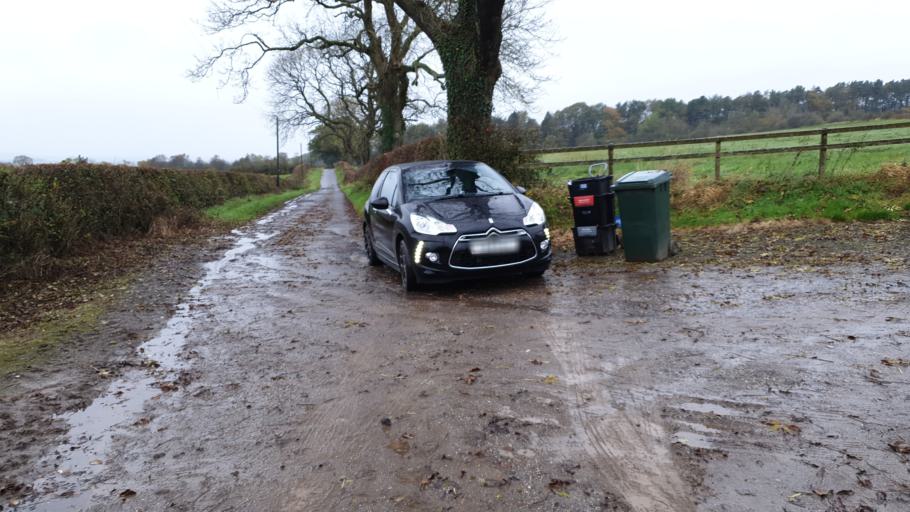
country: GB
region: Scotland
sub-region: East Ayrshire
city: Newmilns
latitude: 55.6120
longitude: -4.3389
